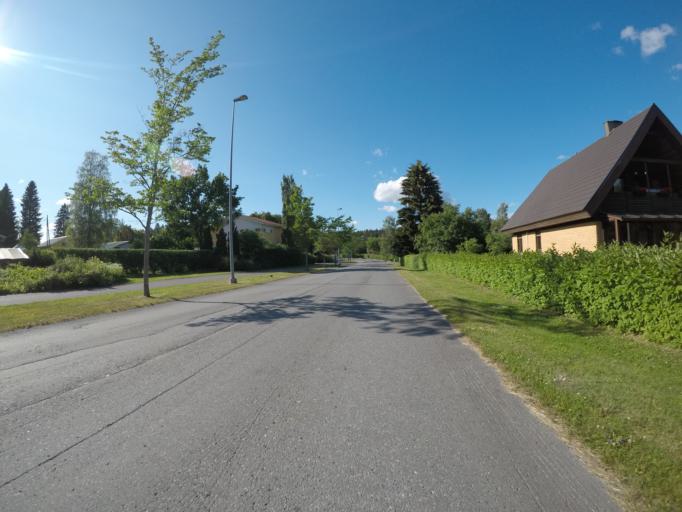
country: FI
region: Haeme
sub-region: Haemeenlinna
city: Haemeenlinna
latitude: 61.0186
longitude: 24.5020
